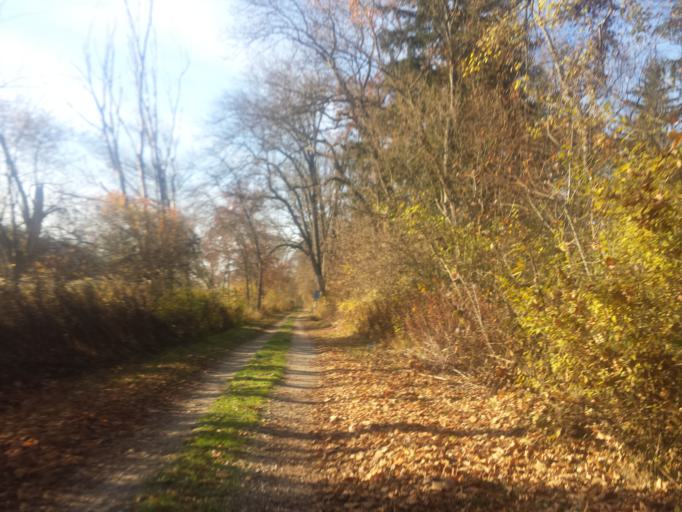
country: DE
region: Bavaria
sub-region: Upper Bavaria
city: Weichering
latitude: 48.7396
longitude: 11.3238
